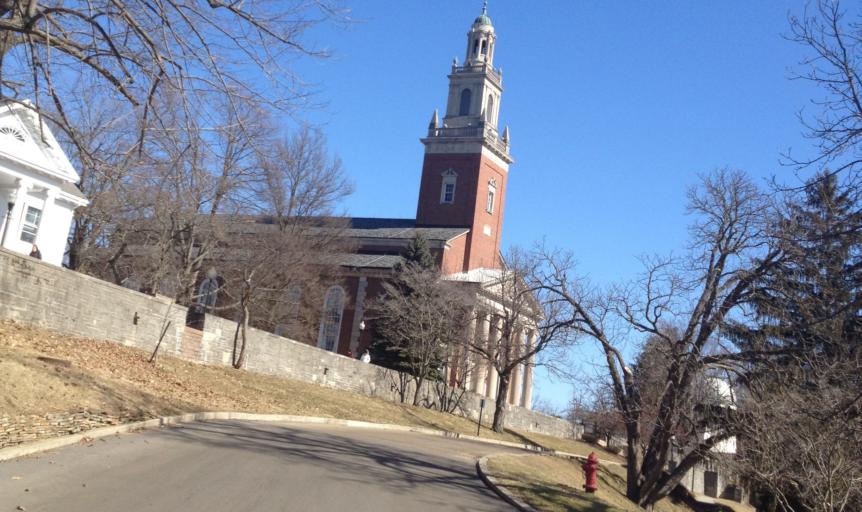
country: US
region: Ohio
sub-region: Licking County
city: Granville
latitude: 40.0708
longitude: -82.5227
